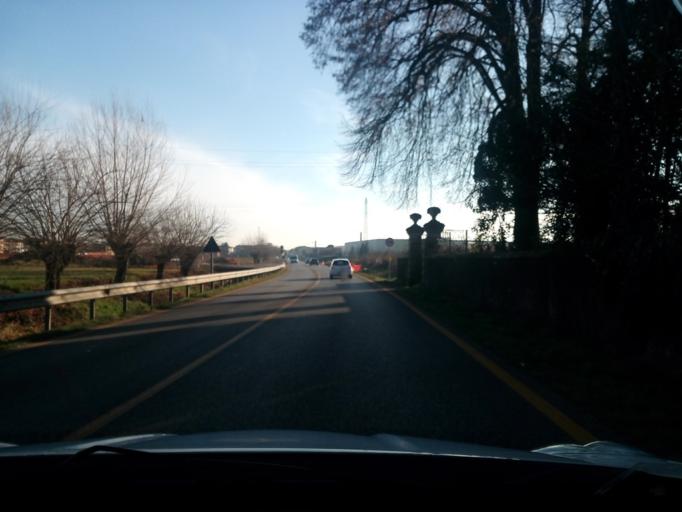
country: IT
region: Veneto
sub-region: Provincia di Vicenza
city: Villaverla
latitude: 45.6630
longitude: 11.4911
